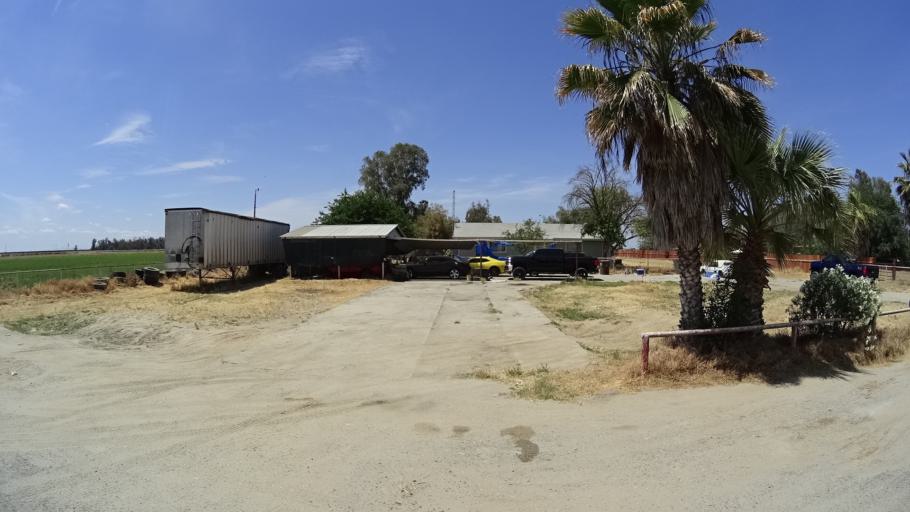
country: US
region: California
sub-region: Kings County
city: Home Garden
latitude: 36.2655
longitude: -119.6727
